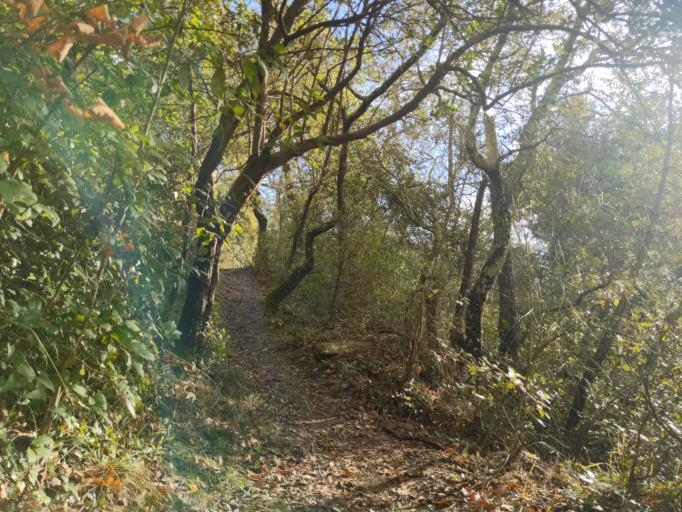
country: FR
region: Provence-Alpes-Cote d'Azur
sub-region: Departement du Var
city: Bagnols-en-Foret
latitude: 43.5395
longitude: 6.7057
